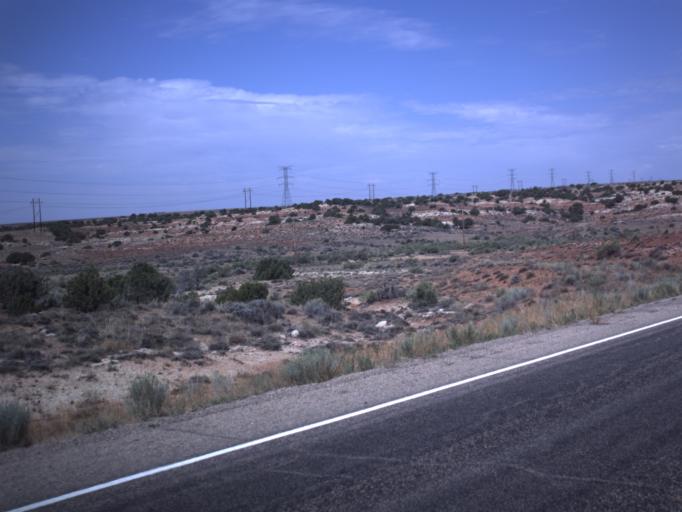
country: US
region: Utah
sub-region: Uintah County
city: Naples
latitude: 40.1638
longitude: -109.3127
